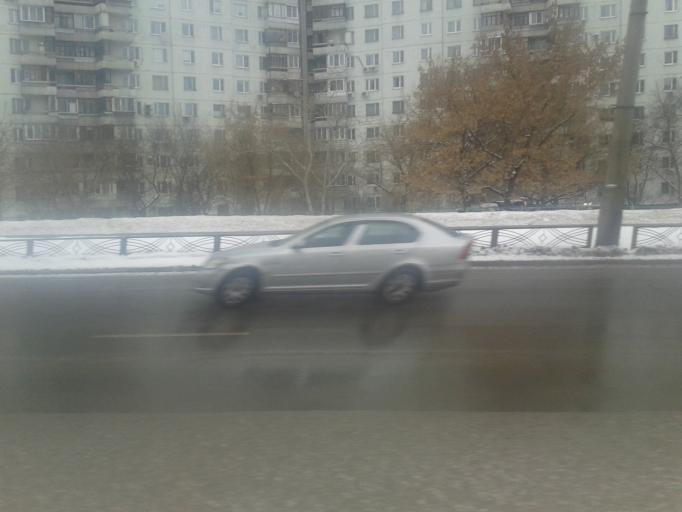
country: RU
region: Moscow
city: Strogino
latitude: 55.8118
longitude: 37.4012
